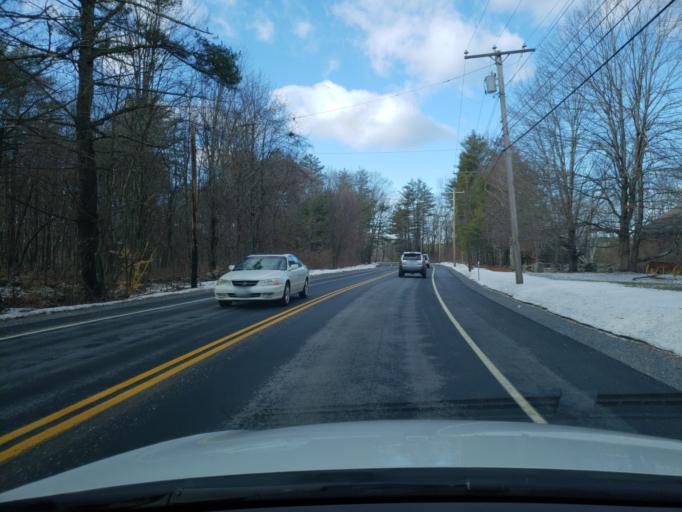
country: US
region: New Hampshire
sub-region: Hillsborough County
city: Goffstown
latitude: 43.0151
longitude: -71.5648
